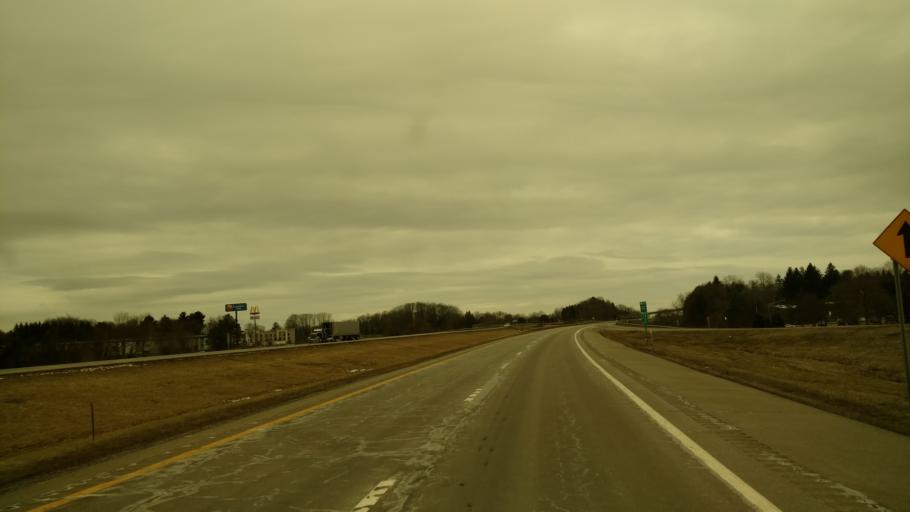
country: US
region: New York
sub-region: Chautauqua County
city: Jamestown
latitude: 42.1223
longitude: -79.2374
